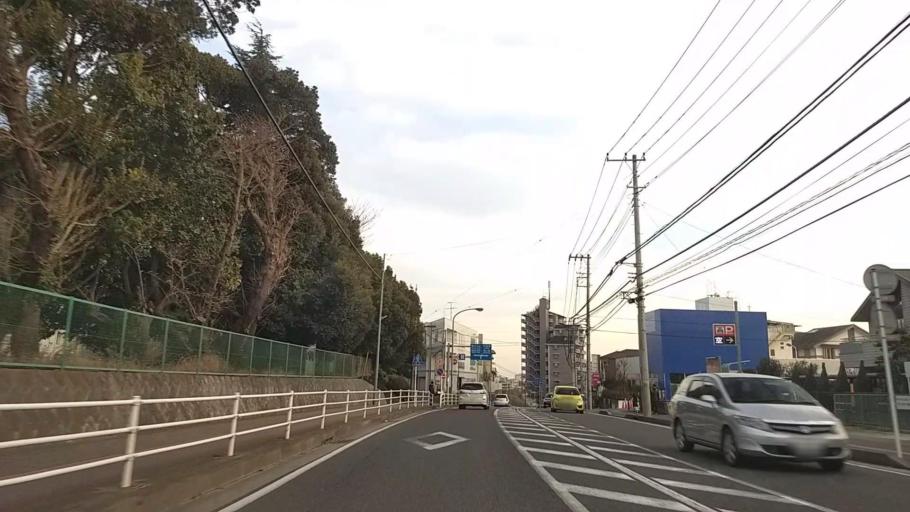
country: JP
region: Kanagawa
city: Atsugi
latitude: 35.4452
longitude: 139.3492
